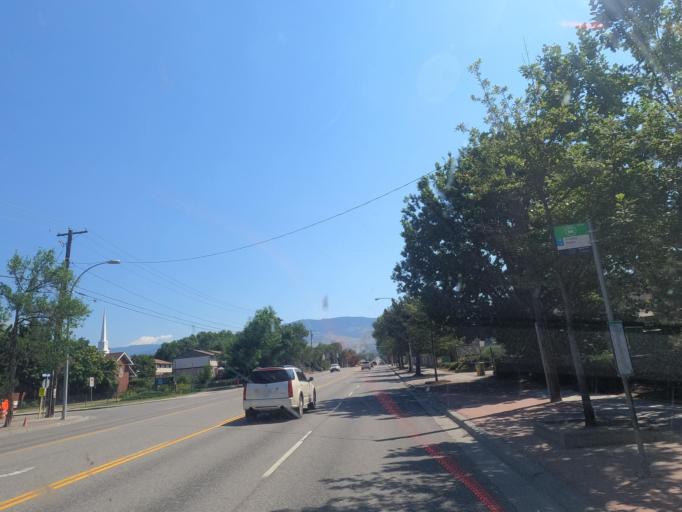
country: CA
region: British Columbia
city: Kelowna
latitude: 49.8890
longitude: -119.4130
